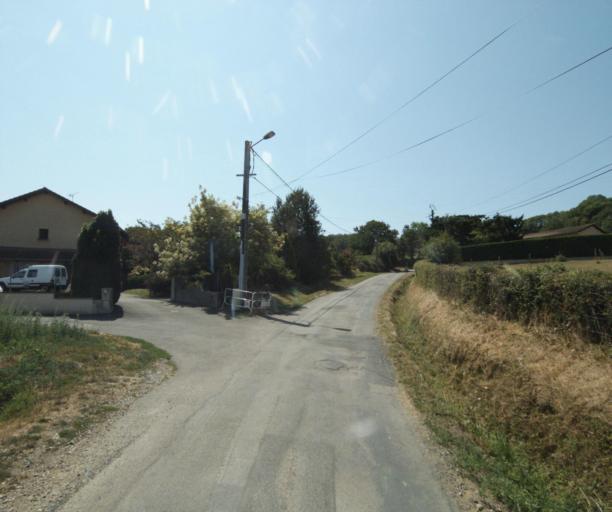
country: FR
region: Rhone-Alpes
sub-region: Departement du Rhone
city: Saint-Pierre-la-Palud
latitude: 45.7929
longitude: 4.6216
